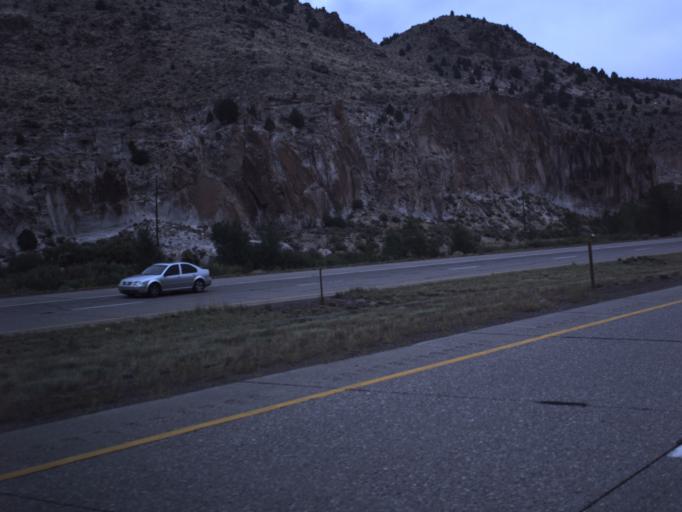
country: US
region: Utah
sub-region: Sevier County
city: Monroe
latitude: 38.5783
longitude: -112.3287
